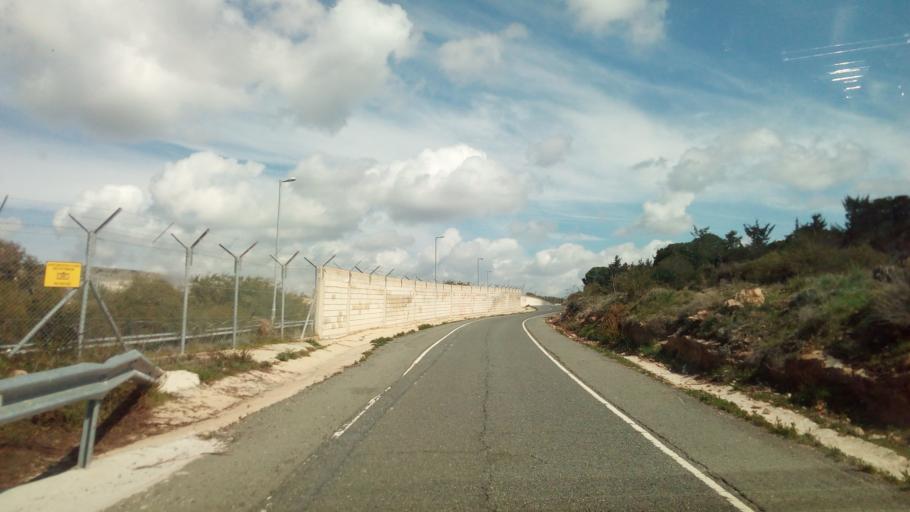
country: CY
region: Pafos
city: Mesogi
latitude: 34.7484
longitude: 32.5476
